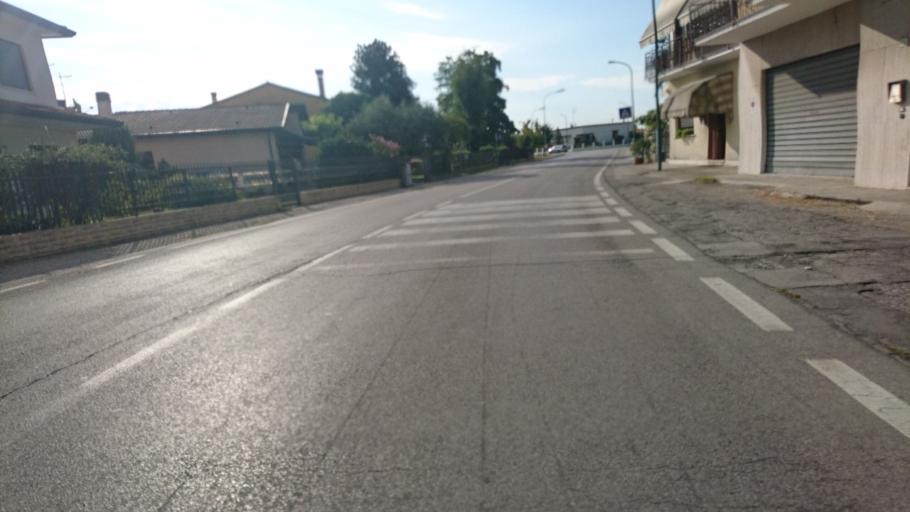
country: IT
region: Veneto
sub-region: Provincia di Venezia
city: Mira Taglio
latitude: 45.4243
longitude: 12.1523
